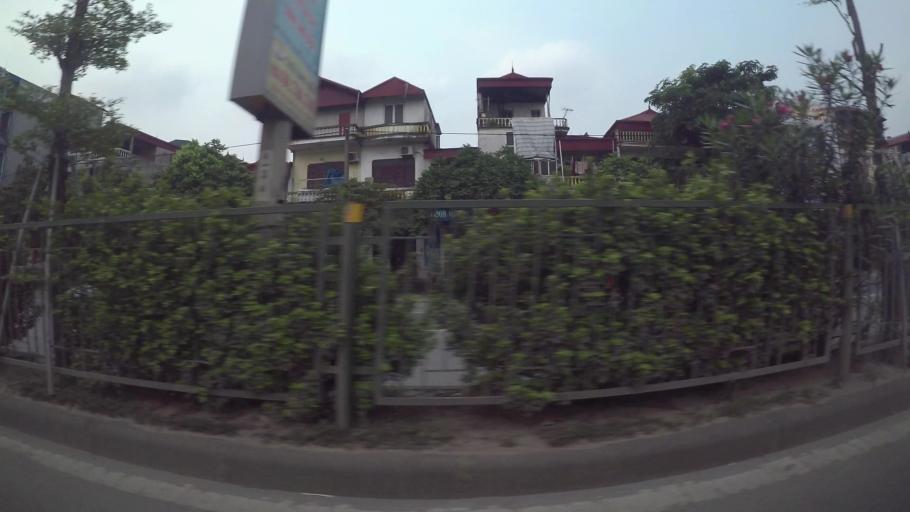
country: VN
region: Ha Noi
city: Trau Quy
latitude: 21.0294
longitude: 105.9160
